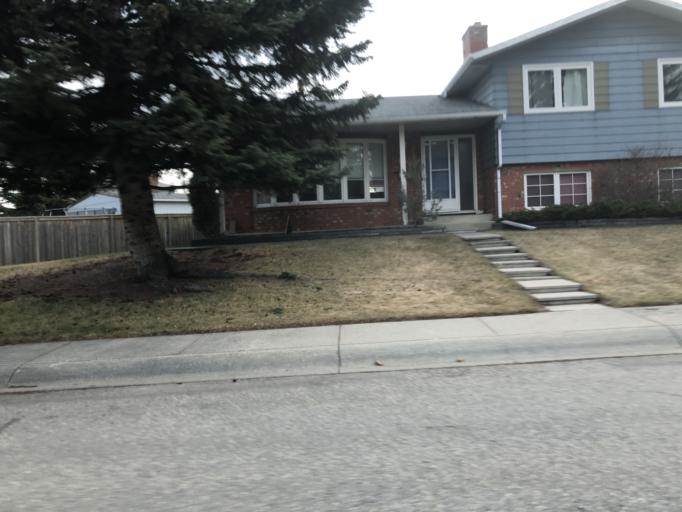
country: CA
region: Alberta
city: Calgary
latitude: 50.9305
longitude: -114.0431
